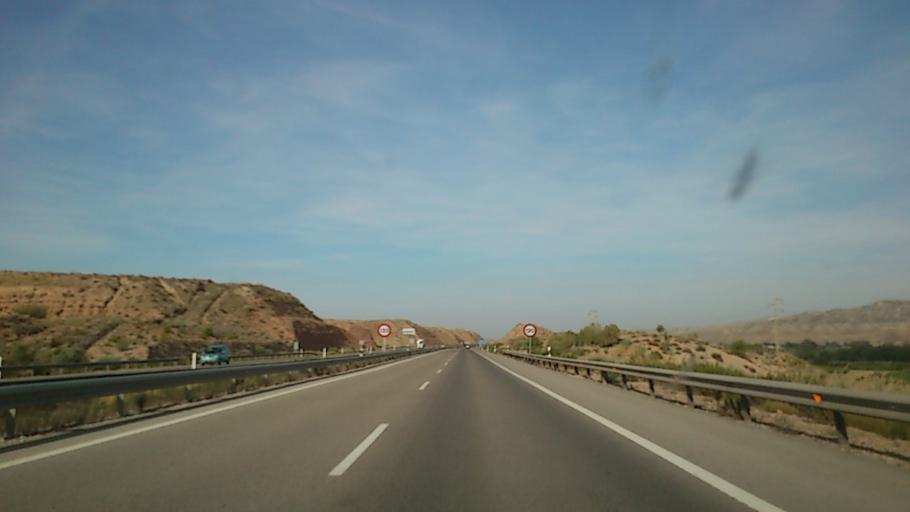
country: ES
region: Aragon
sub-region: Provincia de Zaragoza
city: Botorrita
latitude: 41.5223
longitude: -1.0299
